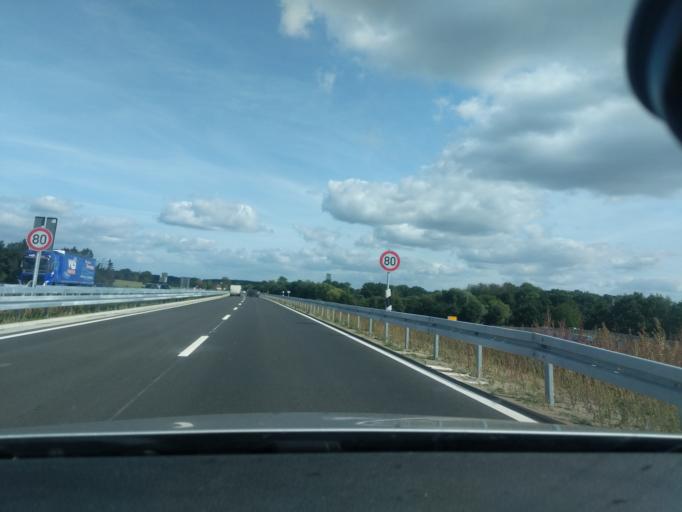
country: DE
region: Lower Saxony
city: Belm
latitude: 52.3097
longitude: 8.1256
